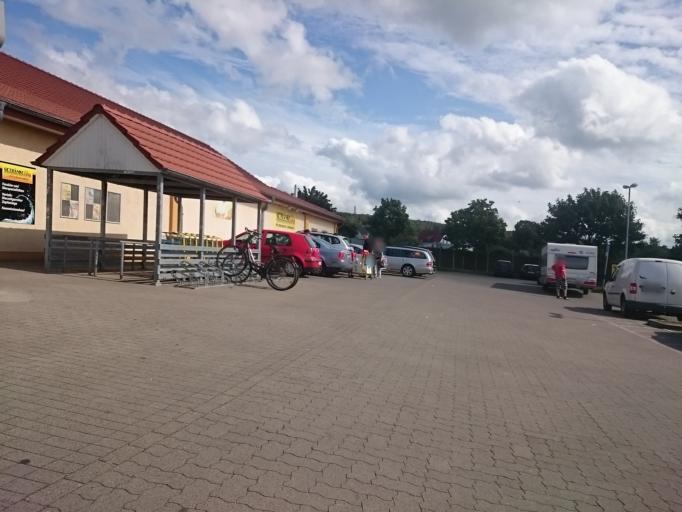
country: DE
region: Mecklenburg-Vorpommern
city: Koserow
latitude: 54.0468
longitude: 14.0017
